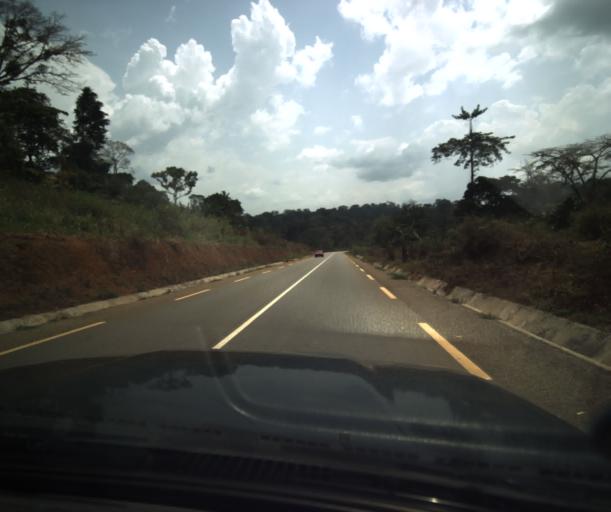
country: CM
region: Centre
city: Mbankomo
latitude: 3.6743
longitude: 11.3501
